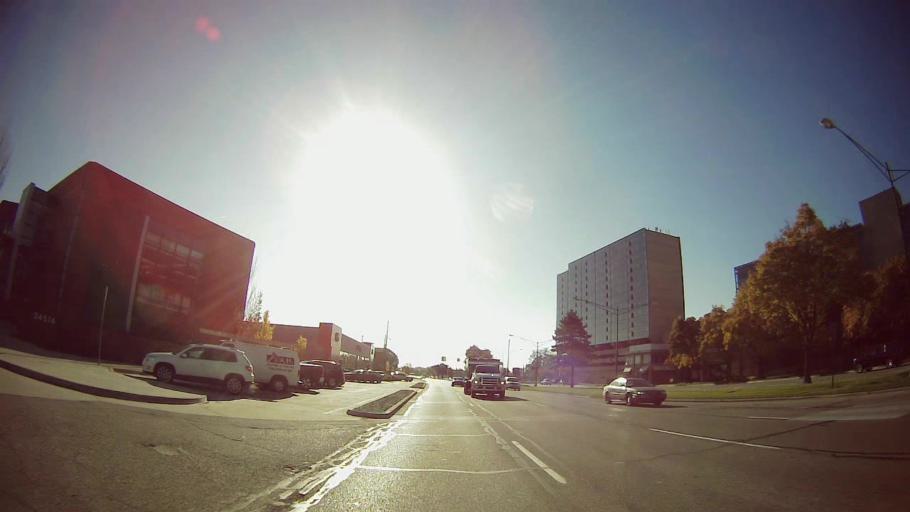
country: US
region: Michigan
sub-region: Oakland County
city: Birmingham
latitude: 42.5439
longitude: -83.2096
